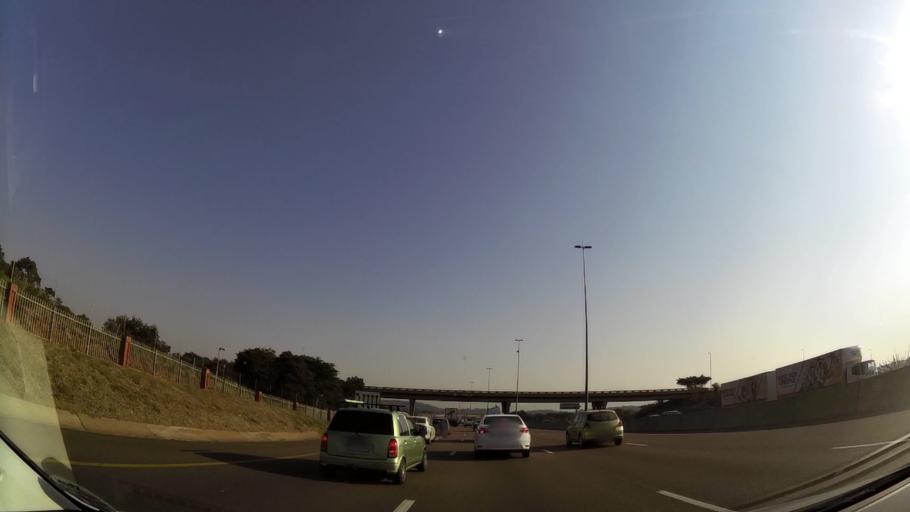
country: ZA
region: Gauteng
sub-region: City of Tshwane Metropolitan Municipality
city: Pretoria
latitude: -25.7499
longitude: 28.2723
